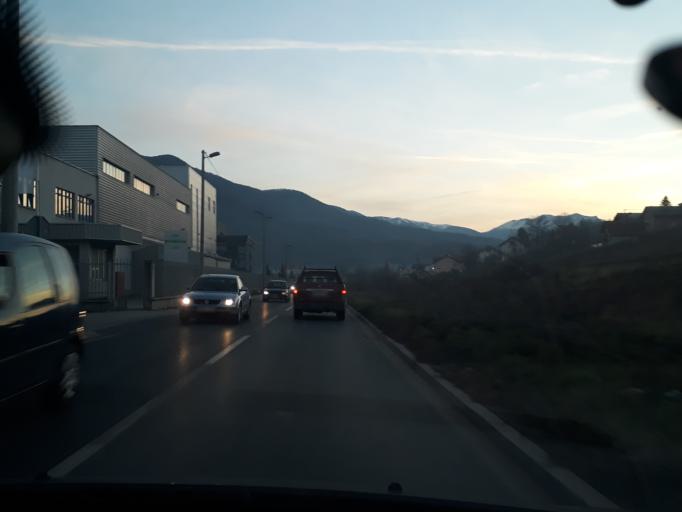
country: BA
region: Federation of Bosnia and Herzegovina
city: Hadzici
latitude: 43.8569
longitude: 18.2501
